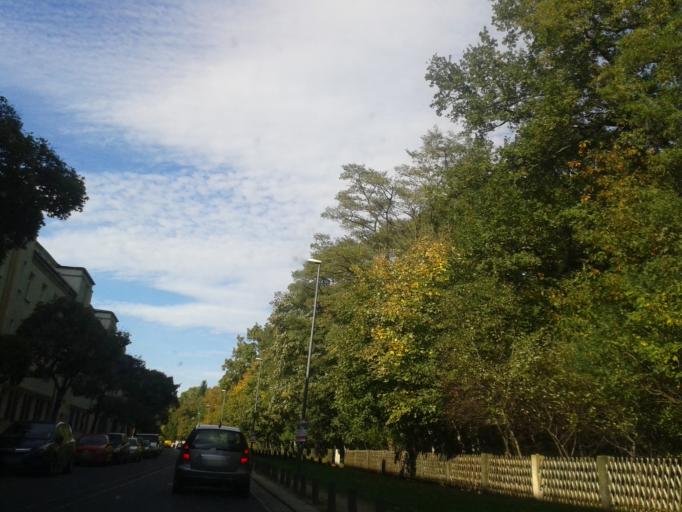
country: DE
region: Saxony
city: Albertstadt
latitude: 51.0828
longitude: 13.7445
